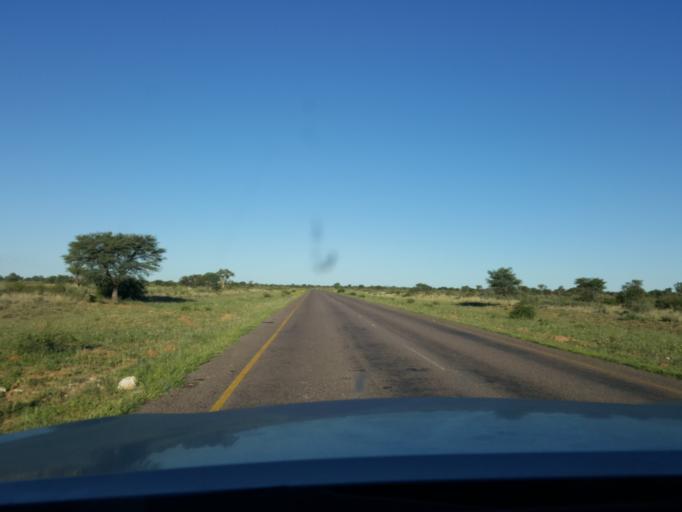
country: BW
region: Southern
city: Khakhea
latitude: -24.3004
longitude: 23.3887
